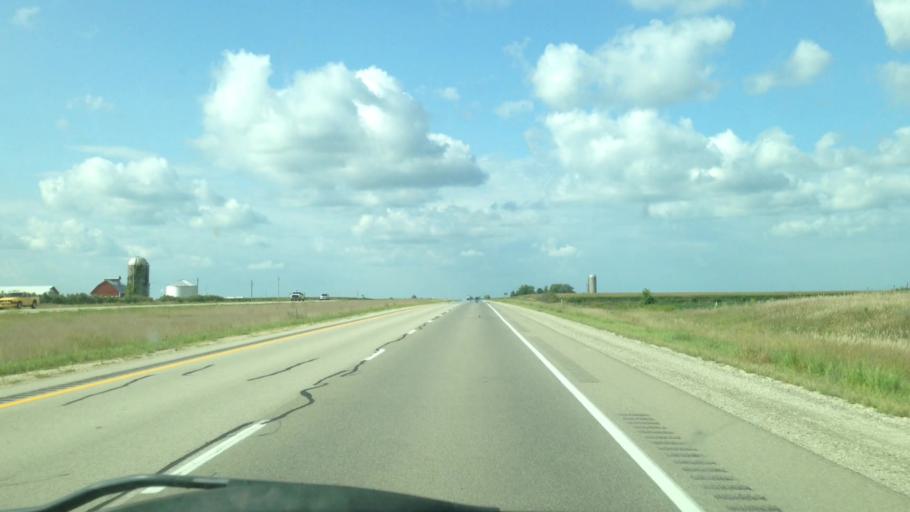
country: US
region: Iowa
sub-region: Henry County
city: Mount Pleasant
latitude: 40.8105
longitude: -91.5641
